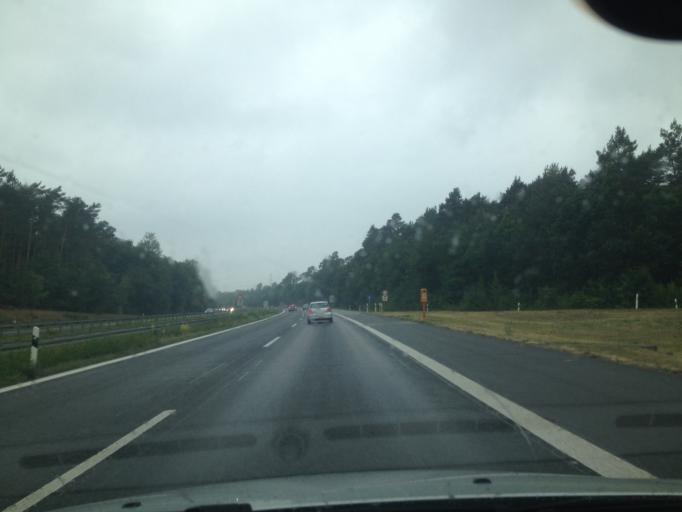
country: DE
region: Bavaria
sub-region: Regierungsbezirk Unterfranken
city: Kahl am Main
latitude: 50.0985
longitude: 9.0288
